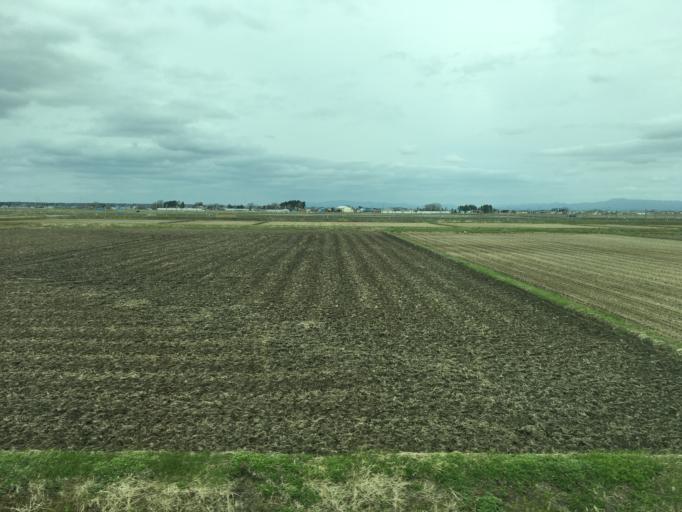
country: JP
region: Aomori
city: Shimokizukuri
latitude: 40.7825
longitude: 140.3300
